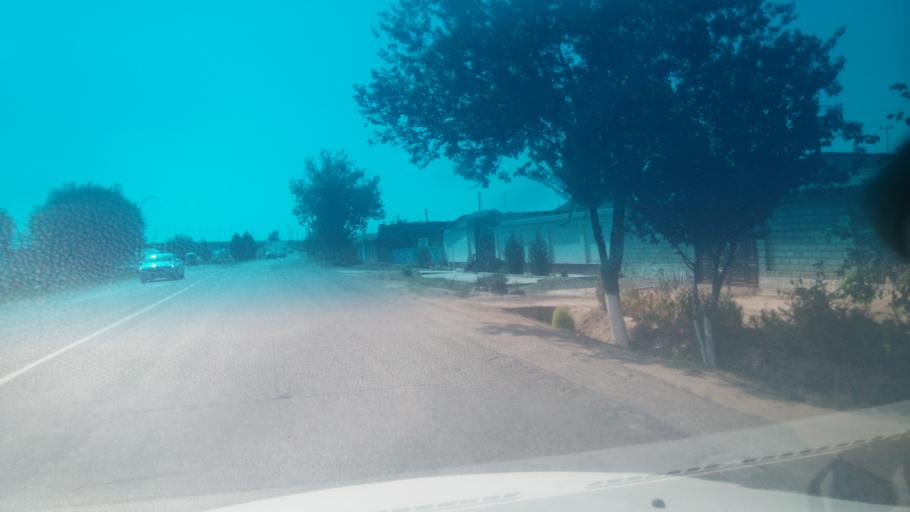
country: UZ
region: Sirdaryo
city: Sirdaryo
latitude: 40.8079
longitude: 68.6760
